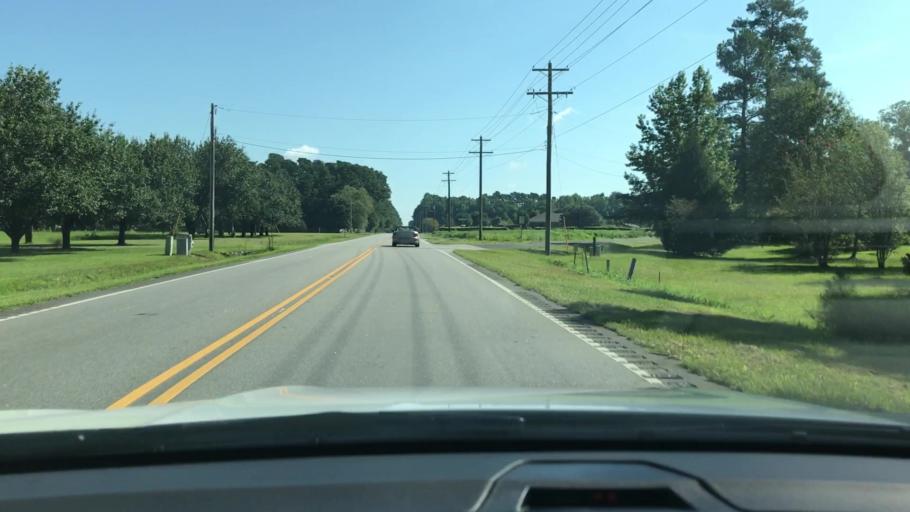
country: US
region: South Carolina
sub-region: Horry County
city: Socastee
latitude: 33.7002
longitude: -79.1091
